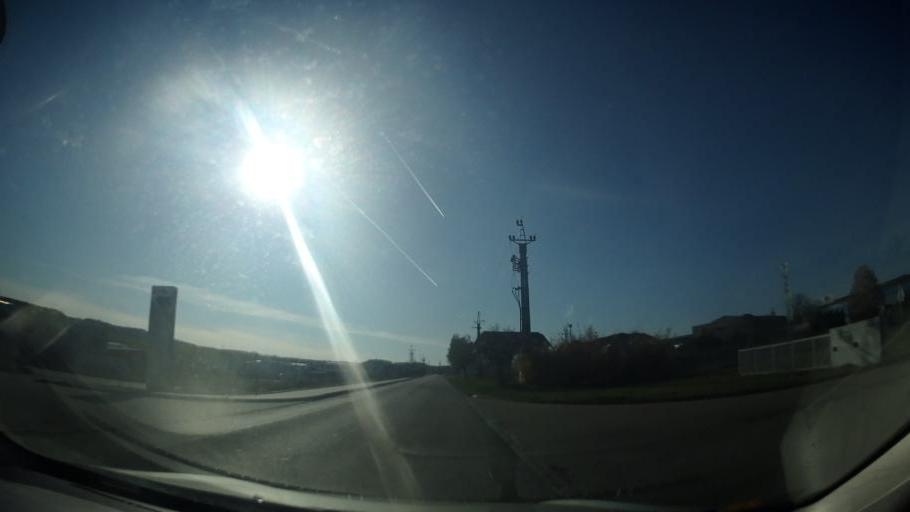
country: CZ
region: South Moravian
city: Moravany
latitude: 49.1447
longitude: 16.5924
